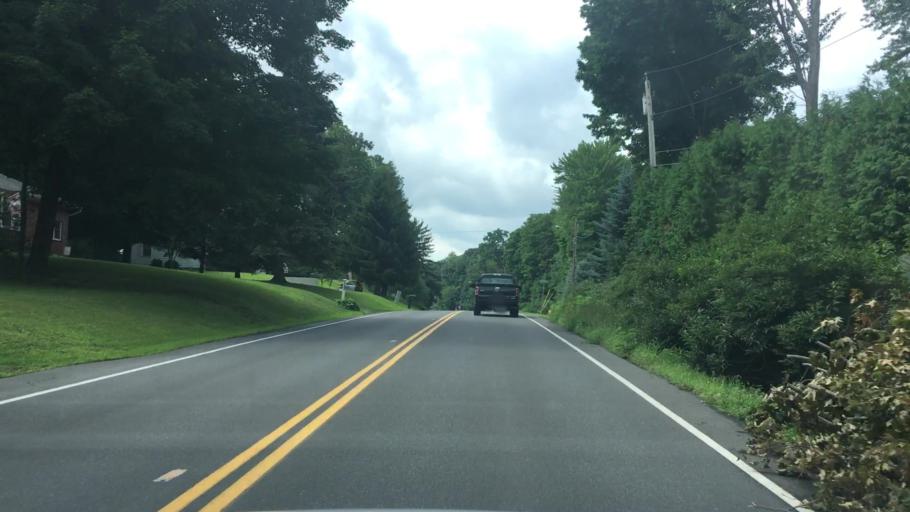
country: US
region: New York
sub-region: Rensselaer County
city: Wynantskill
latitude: 42.6934
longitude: -73.6682
